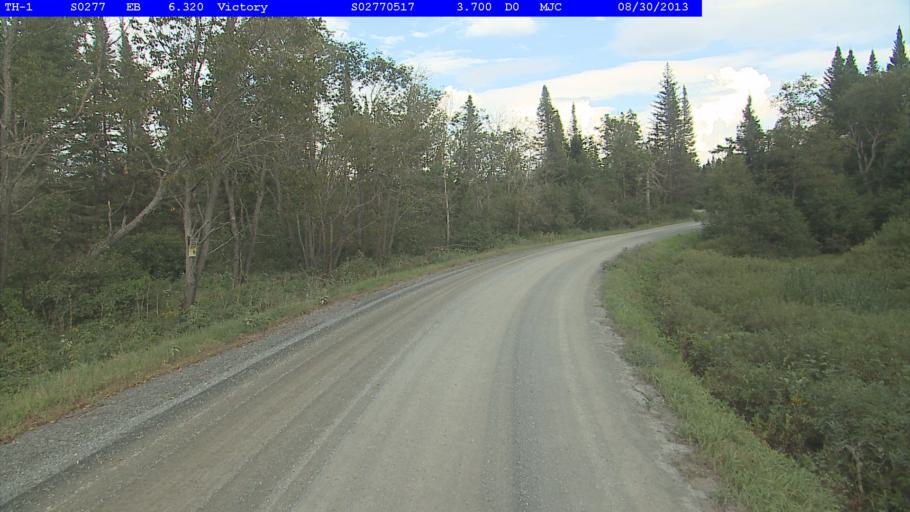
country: US
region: Vermont
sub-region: Caledonia County
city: Lyndonville
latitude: 44.5306
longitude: -71.8046
